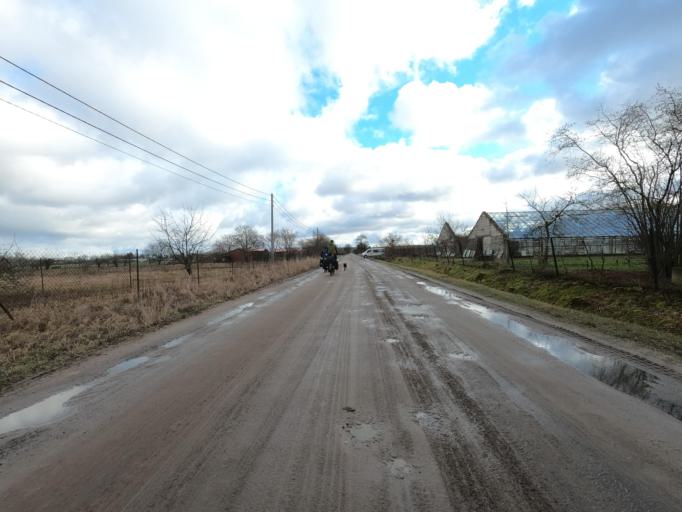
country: PL
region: Greater Poland Voivodeship
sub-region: Powiat pilski
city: Miasteczko Krajenskie
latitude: 53.1137
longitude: 16.9963
